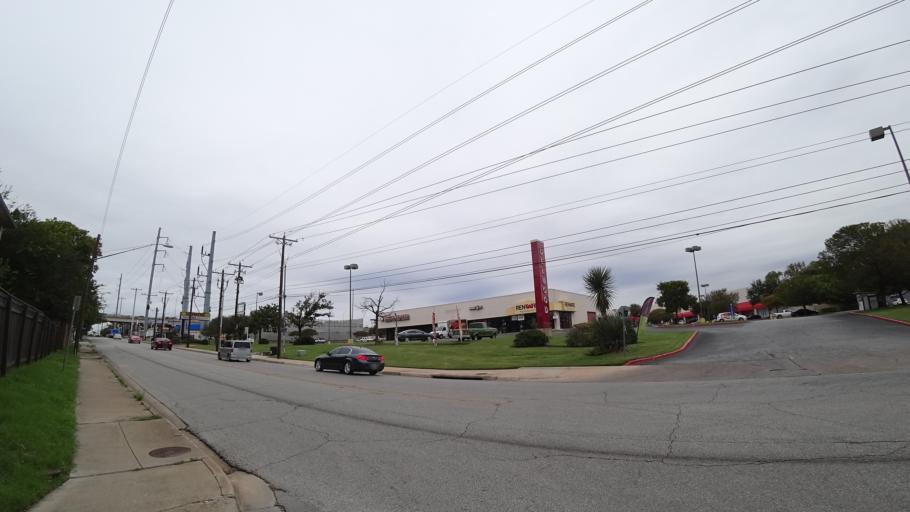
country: US
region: Texas
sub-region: Travis County
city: Austin
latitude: 30.2940
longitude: -97.7180
